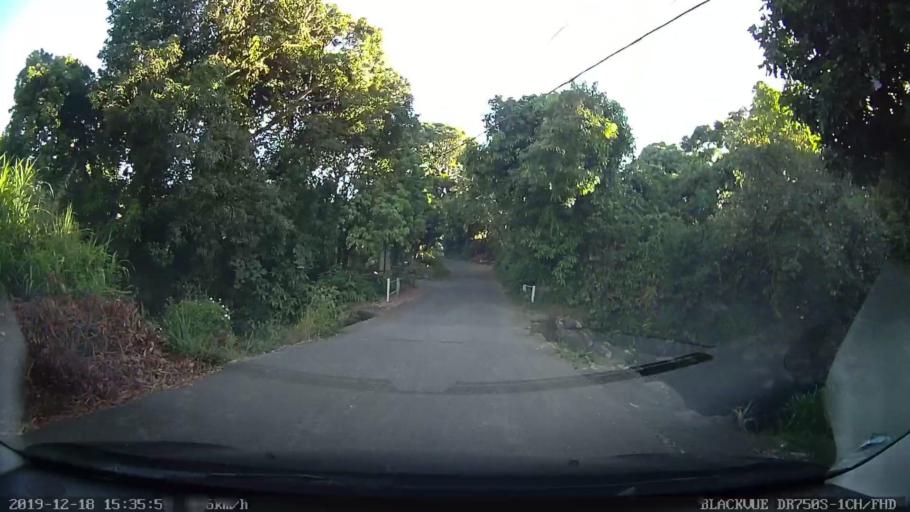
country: RE
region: Reunion
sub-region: Reunion
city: Bras-Panon
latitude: -20.9964
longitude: 55.6631
